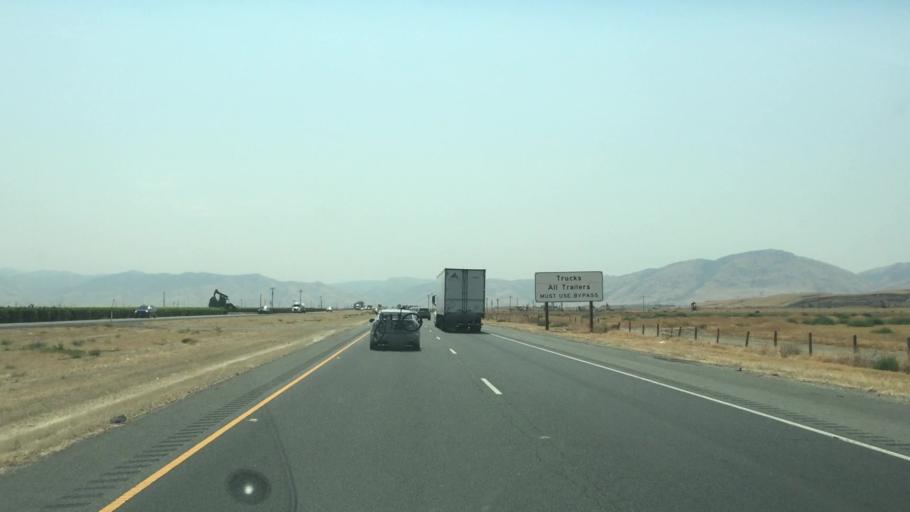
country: US
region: California
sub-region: Kern County
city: Frazier Park
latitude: 35.0314
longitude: -118.9716
